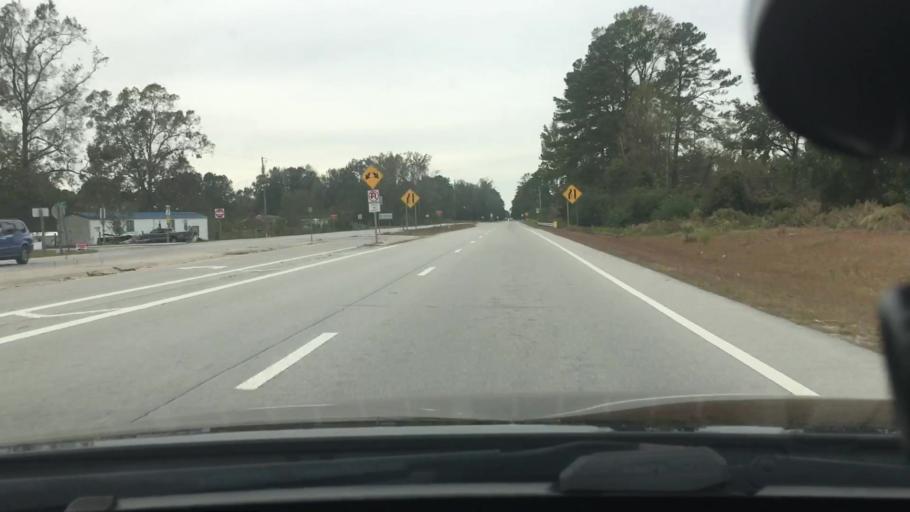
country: US
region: North Carolina
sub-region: Craven County
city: New Bern
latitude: 35.1558
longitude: -77.0362
